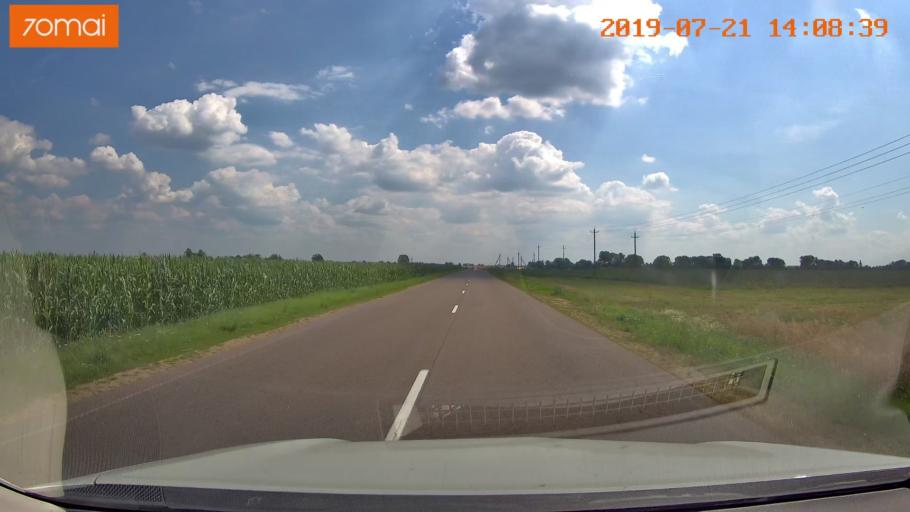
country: BY
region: Grodnenskaya
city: Lyubcha
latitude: 53.6717
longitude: 26.1276
